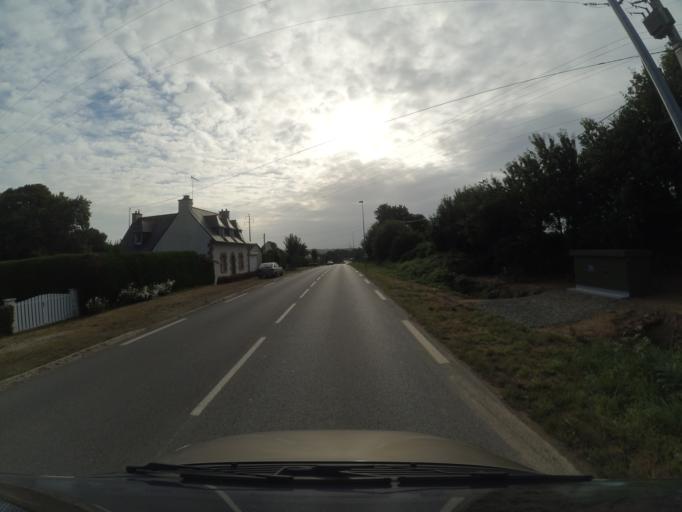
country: FR
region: Brittany
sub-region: Departement des Cotes-d'Armor
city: Graces
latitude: 48.5665
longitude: -3.1863
